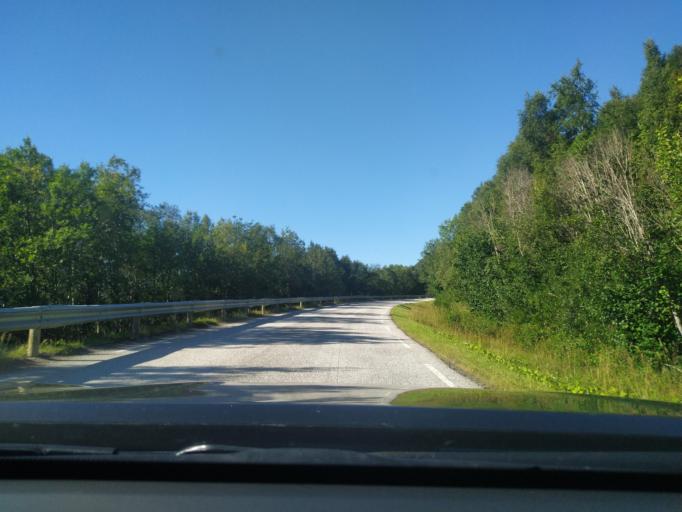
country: NO
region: Troms
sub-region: Dyroy
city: Brostadbotn
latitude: 68.9307
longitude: 17.6661
